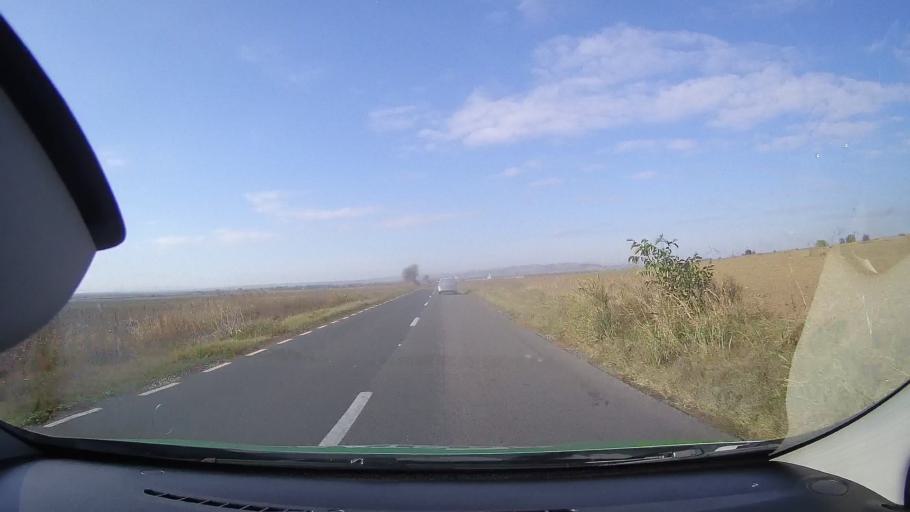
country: RO
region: Tulcea
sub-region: Comuna Valea Nucarilor
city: Iazurile
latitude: 45.0235
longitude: 28.9656
